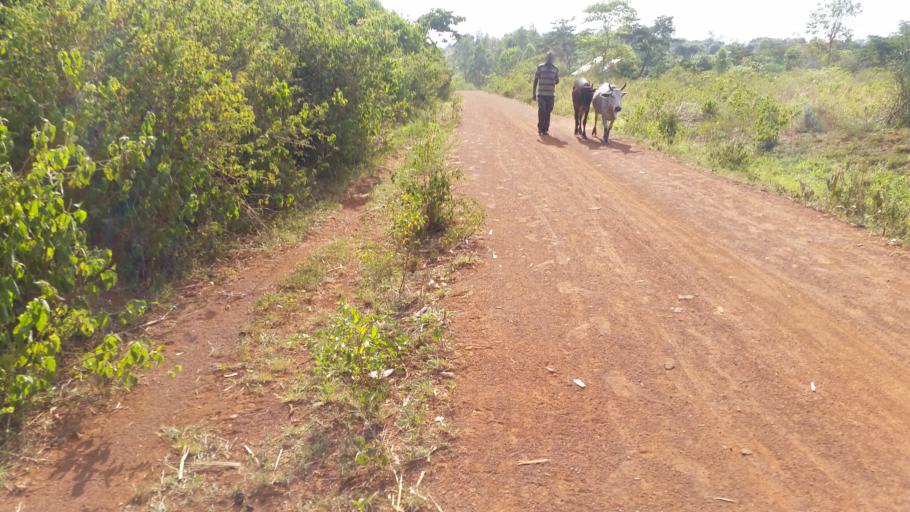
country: UG
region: Eastern Region
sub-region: Busia District
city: Busia
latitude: 0.5500
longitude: 33.9996
